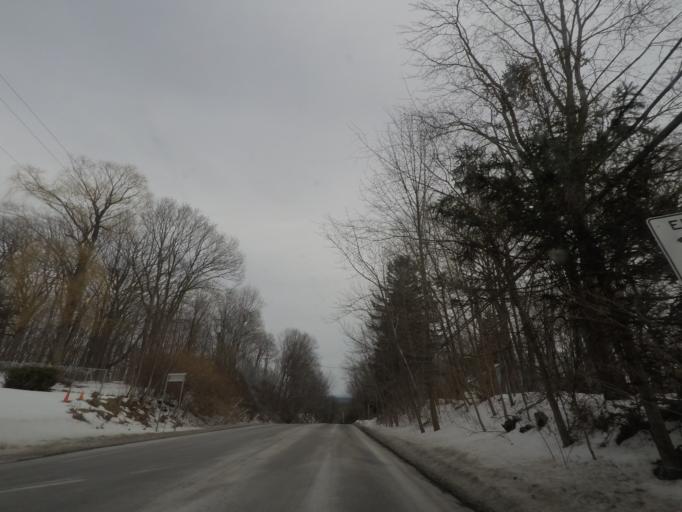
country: US
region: New York
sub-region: Albany County
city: Voorheesville
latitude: 42.5744
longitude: -73.9513
